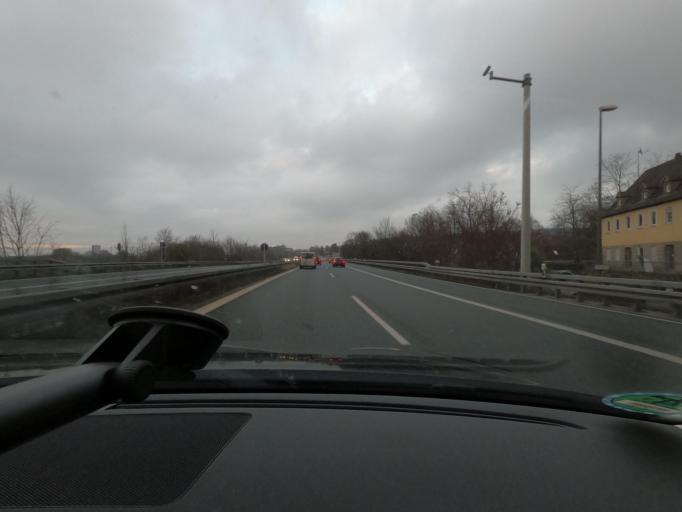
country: DE
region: Bavaria
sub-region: Regierungsbezirk Mittelfranken
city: Mohrendorf
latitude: 49.6116
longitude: 10.9989
